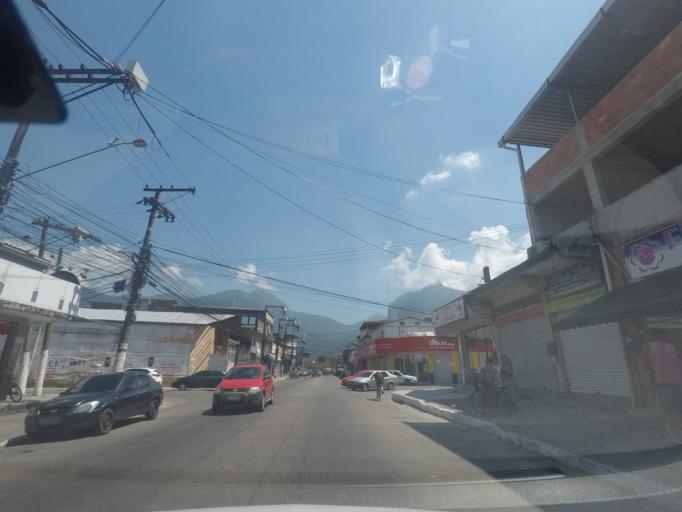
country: BR
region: Rio de Janeiro
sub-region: Petropolis
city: Petropolis
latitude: -22.5882
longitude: -43.1861
